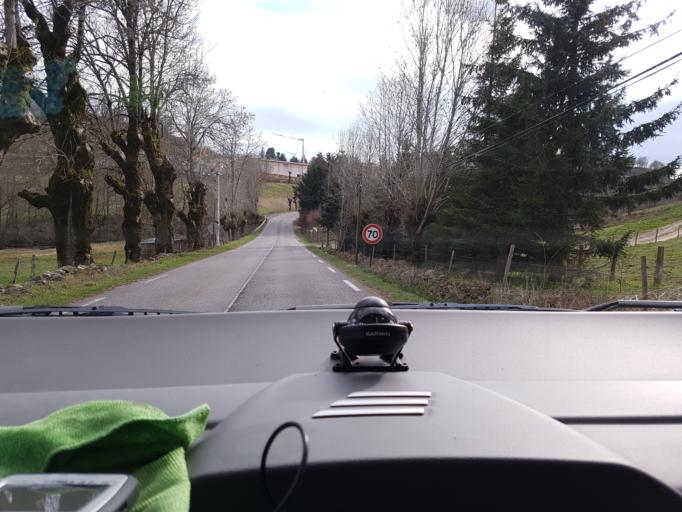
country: FR
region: Midi-Pyrenees
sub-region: Departement de l'Aveyron
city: Laguiole
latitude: 44.6887
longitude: 2.8550
